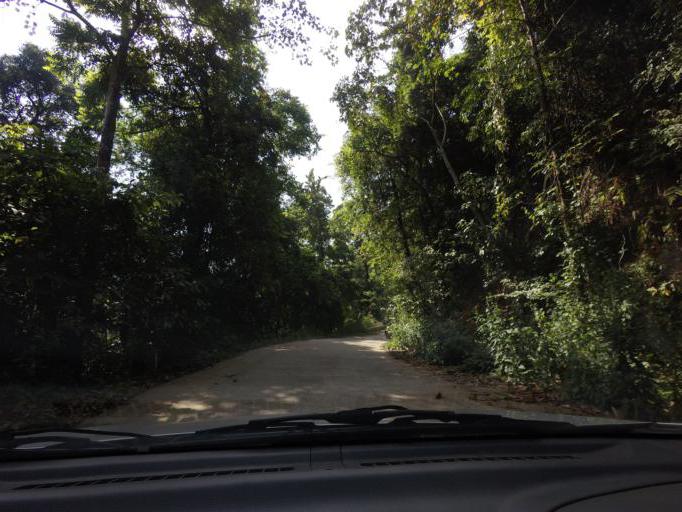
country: IN
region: Karnataka
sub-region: Kodagu
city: Somvarpet
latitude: 12.7243
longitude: 75.6575
